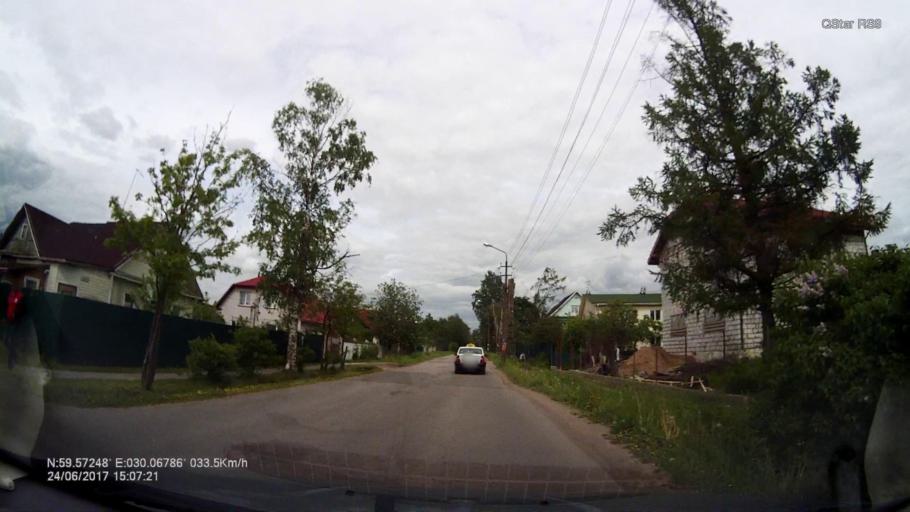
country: RU
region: Leningrad
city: Mariyenburg
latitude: 59.5725
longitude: 30.0680
